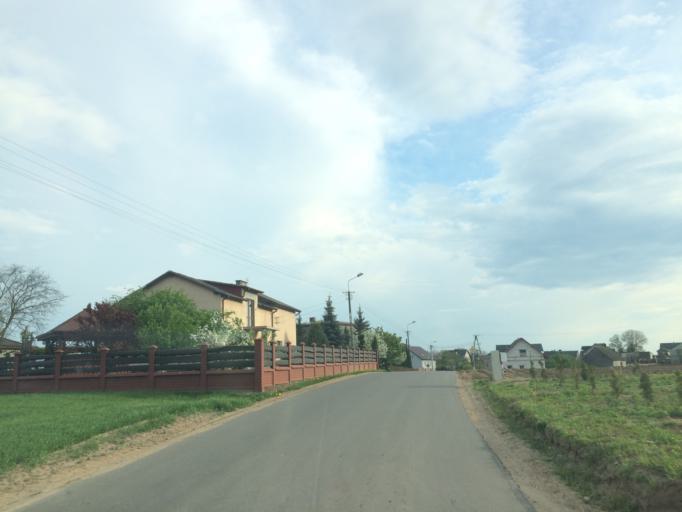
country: PL
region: Kujawsko-Pomorskie
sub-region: Powiat brodnicki
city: Brzozie
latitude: 53.3602
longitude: 19.7104
